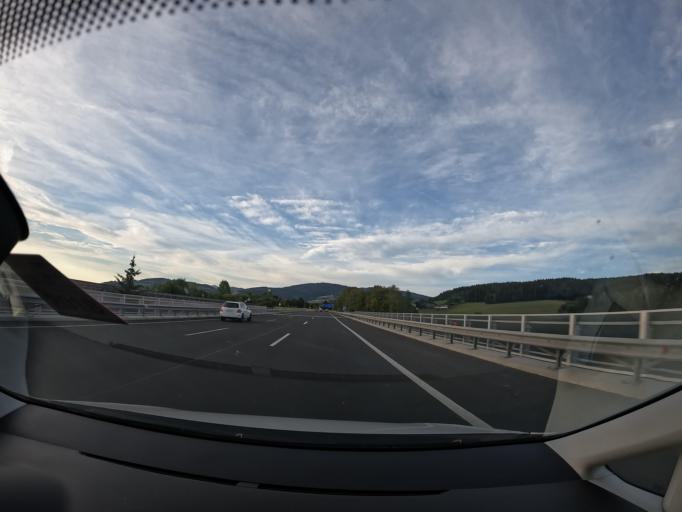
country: AT
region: Carinthia
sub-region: Politischer Bezirk Wolfsberg
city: Bad Sankt Leonhard im Lavanttal
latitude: 46.9322
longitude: 14.8205
